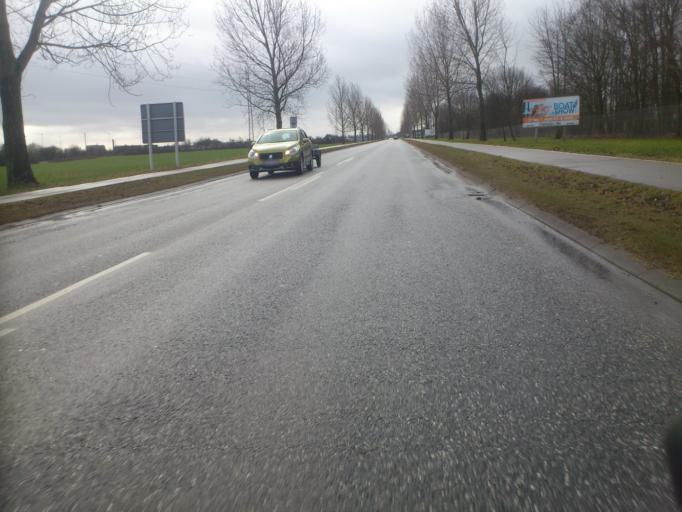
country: DK
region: South Denmark
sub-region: Fredericia Kommune
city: Fredericia
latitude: 55.5992
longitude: 9.7574
